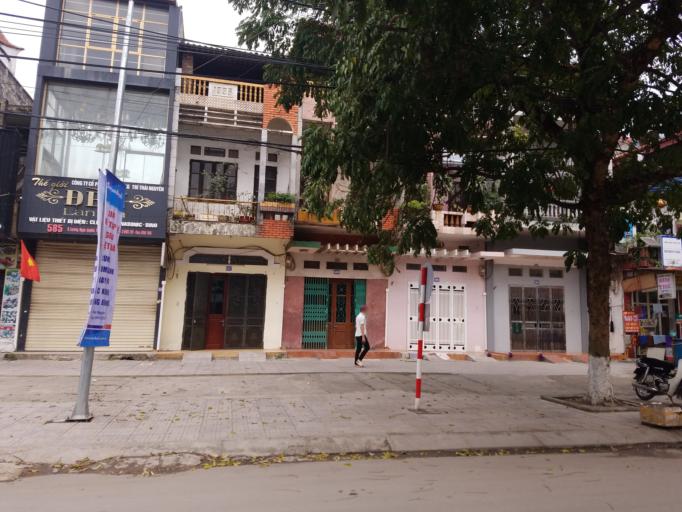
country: VN
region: Thai Nguyen
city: Thanh Pho Thai Nguyen
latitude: 21.5837
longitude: 105.8344
